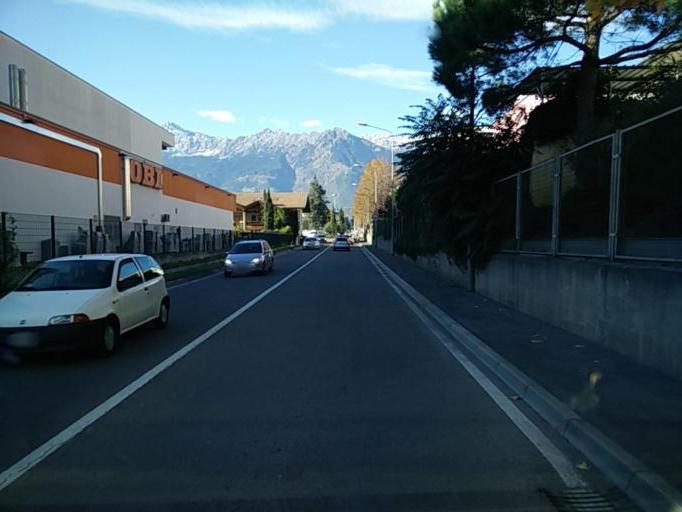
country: IT
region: Trentino-Alto Adige
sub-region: Bolzano
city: Sinigo
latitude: 46.6325
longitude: 11.1787
